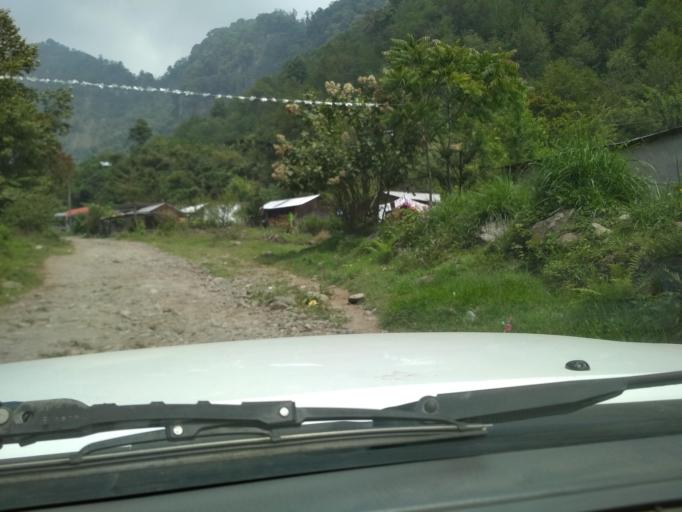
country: MX
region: Veracruz
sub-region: La Perla
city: Metlac Hernandez (Metlac Primero)
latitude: 18.9887
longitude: -97.1162
